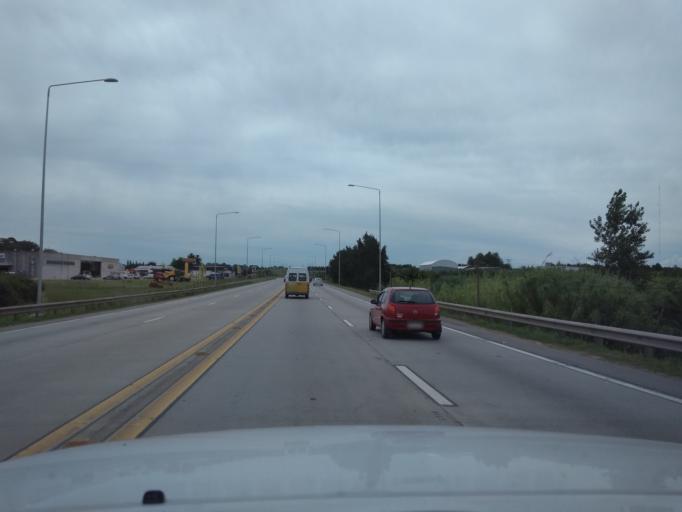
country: UY
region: Canelones
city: La Paz
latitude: -34.7942
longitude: -56.2050
